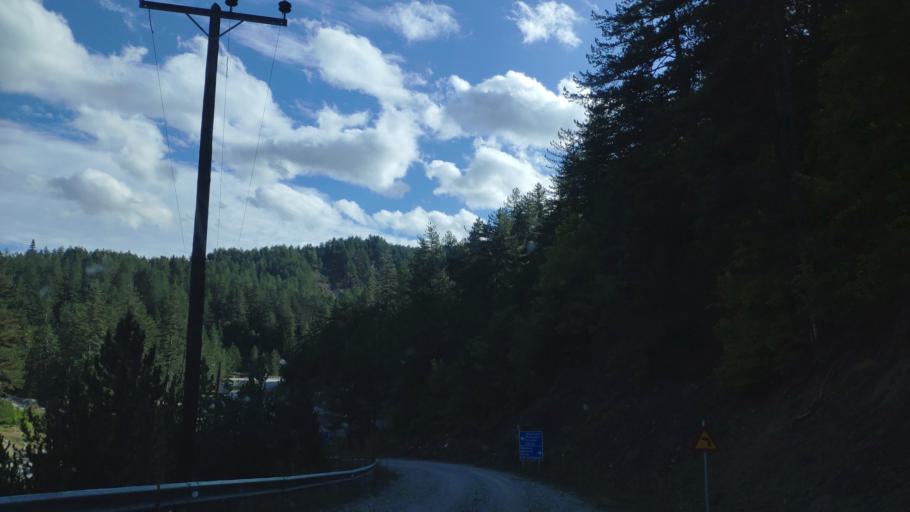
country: AL
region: Korce
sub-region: Rrethi i Devollit
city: Miras
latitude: 40.4121
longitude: 20.8733
